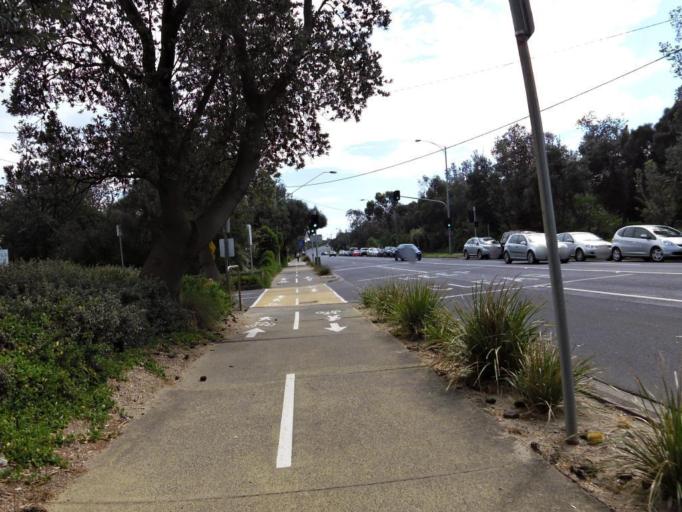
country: AU
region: Victoria
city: Beaumaris
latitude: -37.9917
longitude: 145.0300
